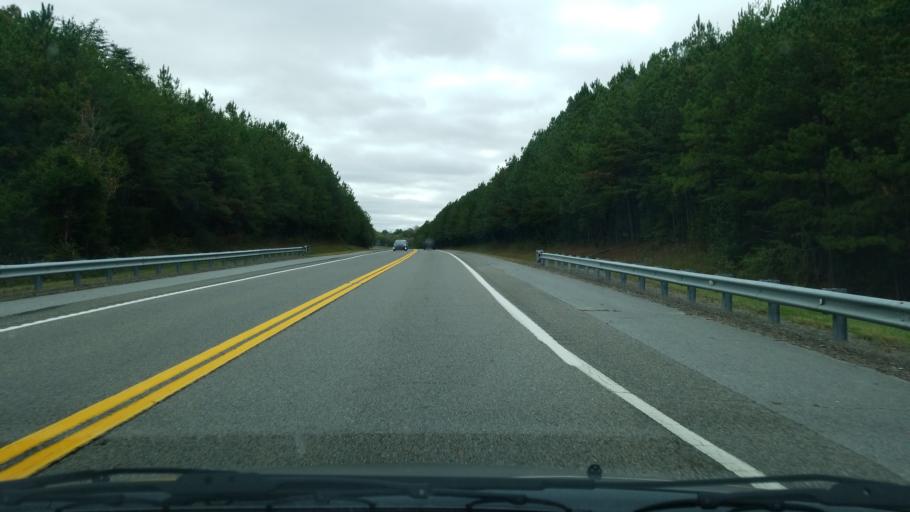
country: US
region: Tennessee
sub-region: Rhea County
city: Dayton
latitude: 35.4437
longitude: -85.0195
